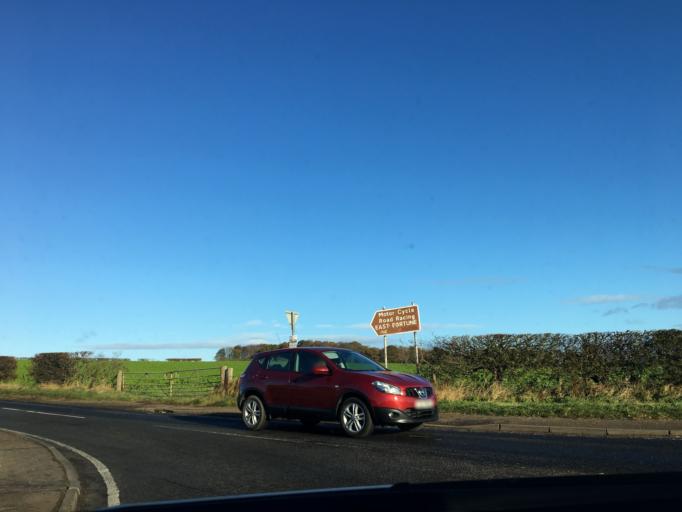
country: GB
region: Scotland
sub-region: East Lothian
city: Haddington
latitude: 55.9705
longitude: -2.7354
